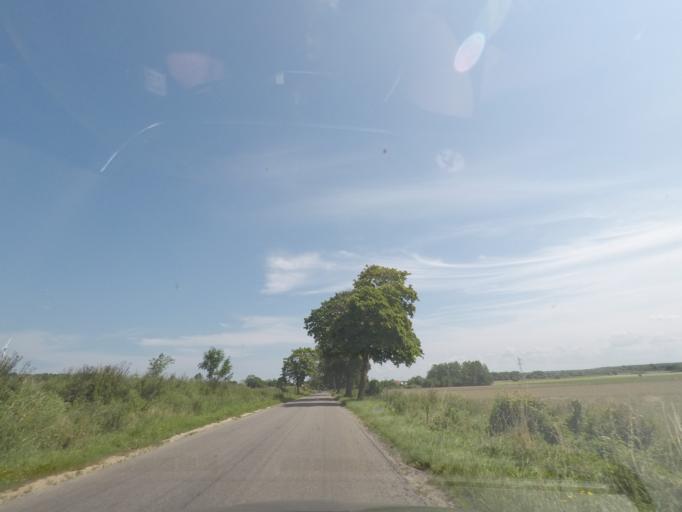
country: PL
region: West Pomeranian Voivodeship
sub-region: Powiat slawienski
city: Darlowo
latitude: 54.4612
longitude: 16.5174
